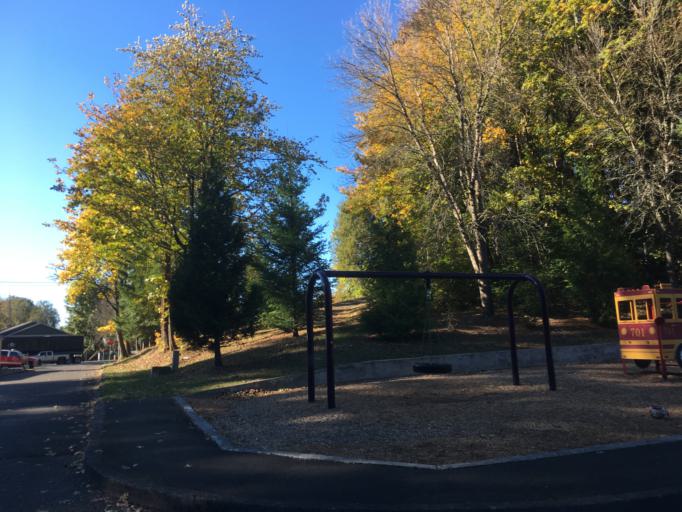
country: US
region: Oregon
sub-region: Multnomah County
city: Gresham
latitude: 45.5018
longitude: -122.3988
